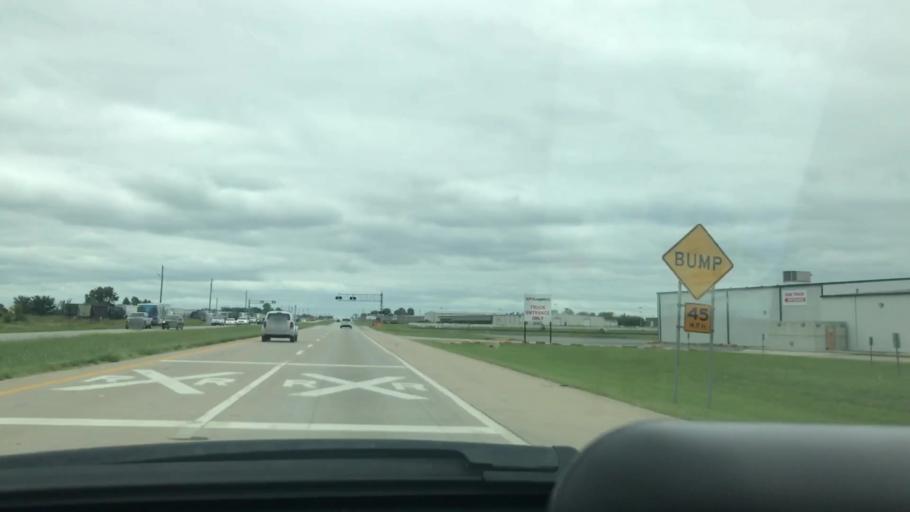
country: US
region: Oklahoma
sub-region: Mayes County
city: Chouteau
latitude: 36.2354
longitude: -95.3386
